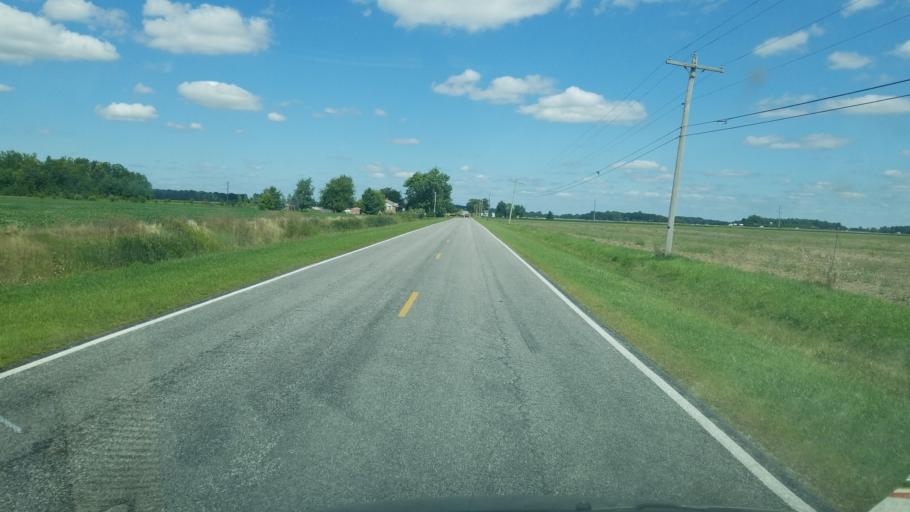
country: US
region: Ohio
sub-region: Fulton County
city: Swanton
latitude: 41.5904
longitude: -83.9407
